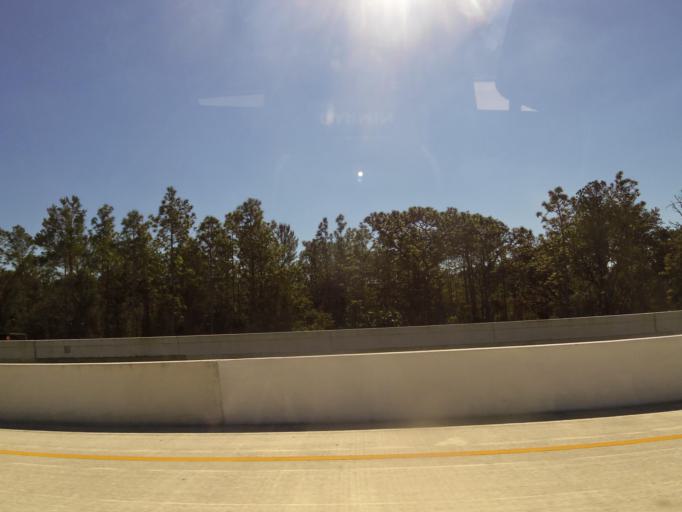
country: US
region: Florida
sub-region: Lake County
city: Mount Plymouth
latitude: 28.8149
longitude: -81.4956
